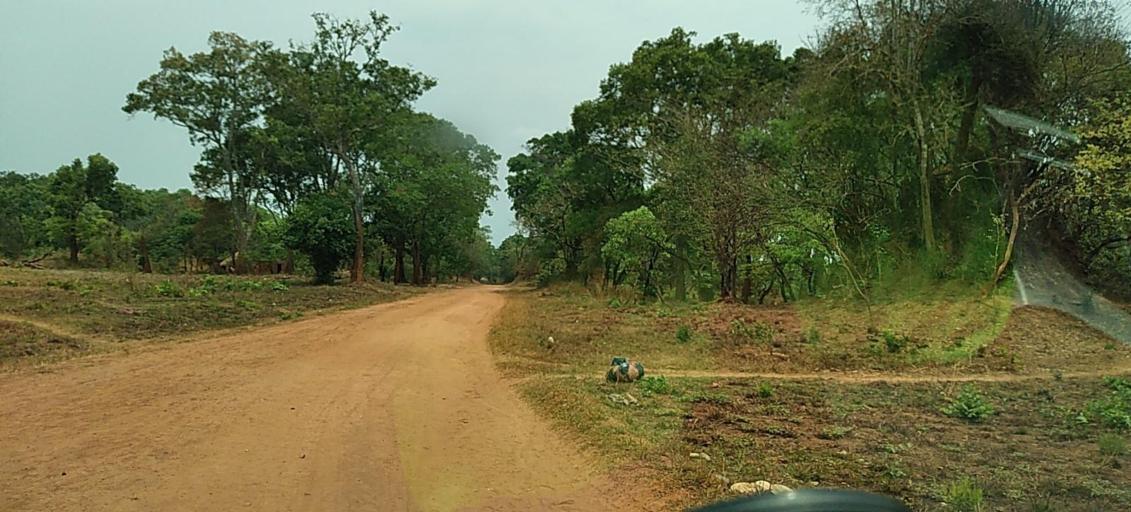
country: ZM
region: North-Western
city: Solwezi
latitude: -12.8033
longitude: 26.5371
